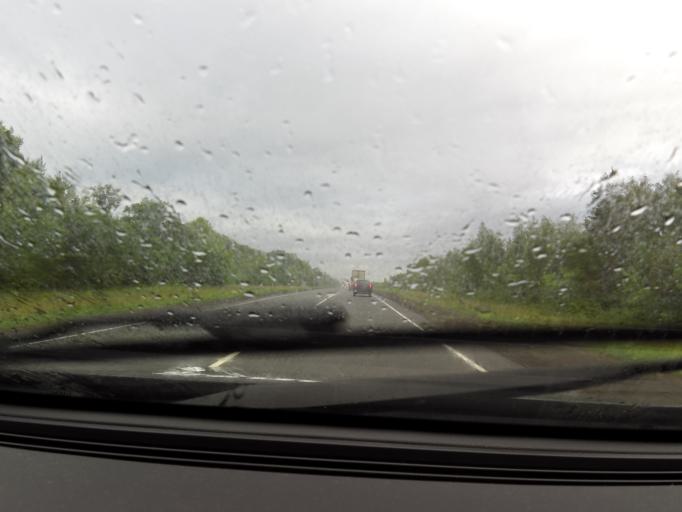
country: RU
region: Chuvashia
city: Kozlovka
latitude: 55.7972
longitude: 48.1034
